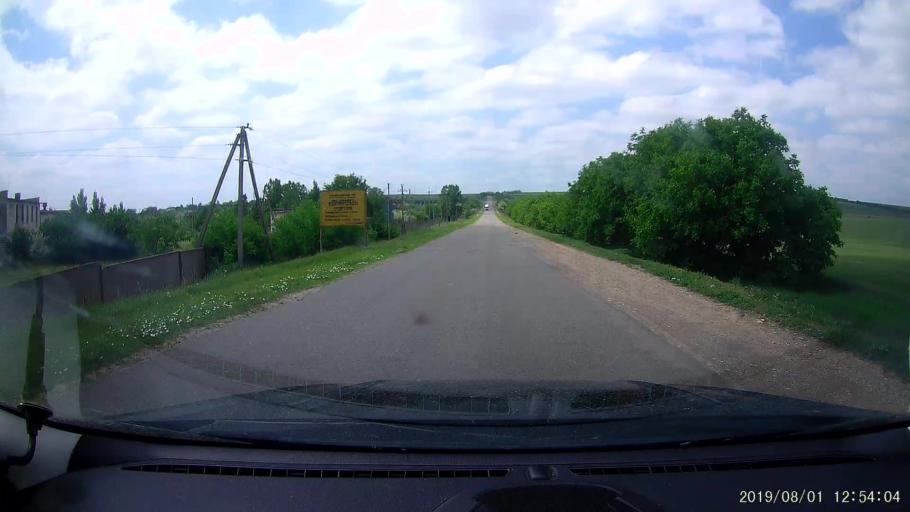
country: UA
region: Odessa
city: Vynohradivka
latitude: 45.6966
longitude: 28.4927
